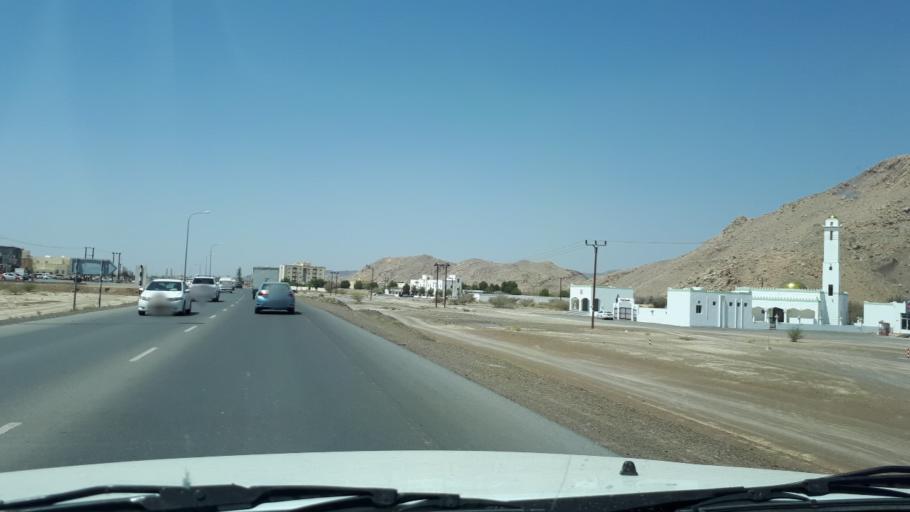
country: OM
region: Muhafazat ad Dakhiliyah
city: Bahla'
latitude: 23.0201
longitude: 57.3306
